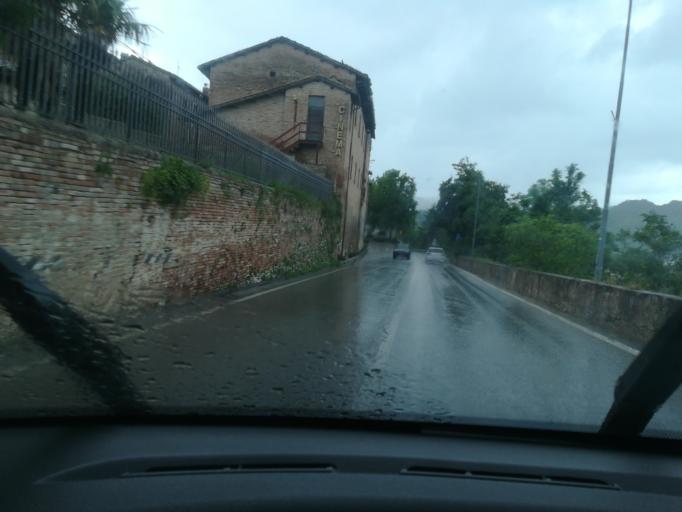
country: IT
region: The Marches
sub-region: Provincia di Macerata
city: Sarnano
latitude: 43.0344
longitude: 13.3011
